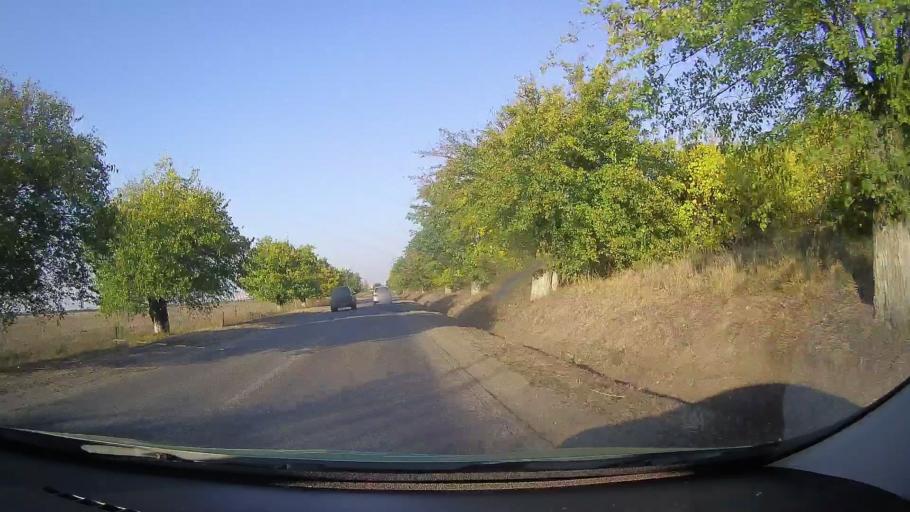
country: RO
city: Masca
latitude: 46.3083
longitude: 21.6755
